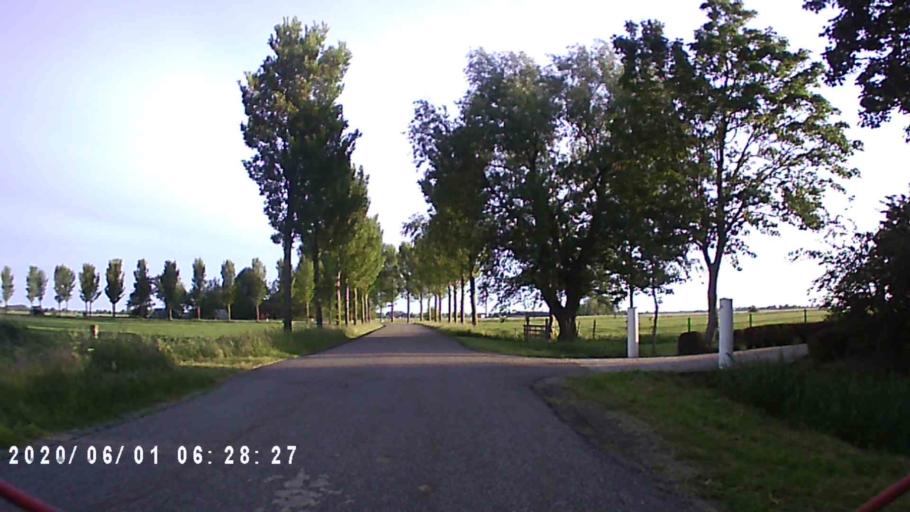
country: NL
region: Friesland
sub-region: Gemeente Kollumerland en Nieuwkruisland
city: Kollum
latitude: 53.2718
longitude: 6.1933
